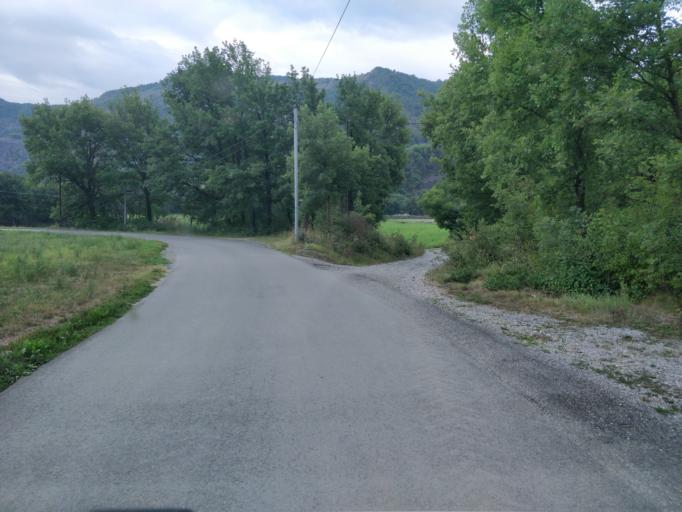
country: FR
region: Provence-Alpes-Cote d'Azur
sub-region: Departement des Alpes-de-Haute-Provence
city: Digne-les-Bains
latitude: 44.1330
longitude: 6.2490
